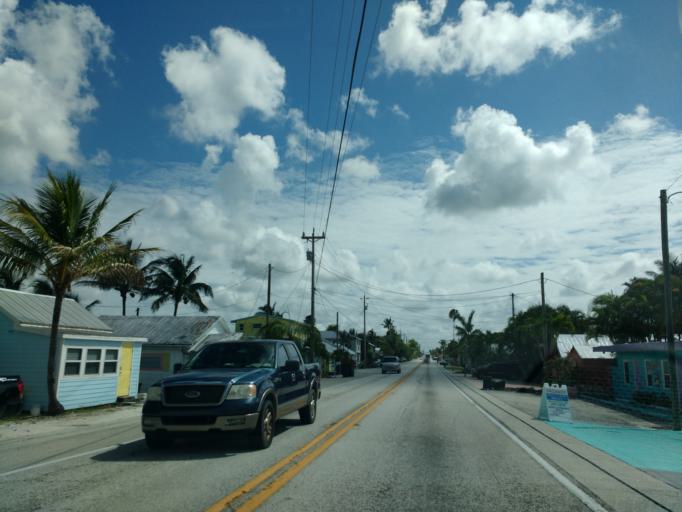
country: US
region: Florida
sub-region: Lee County
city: Pine Island Center
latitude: 26.6263
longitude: -82.0736
